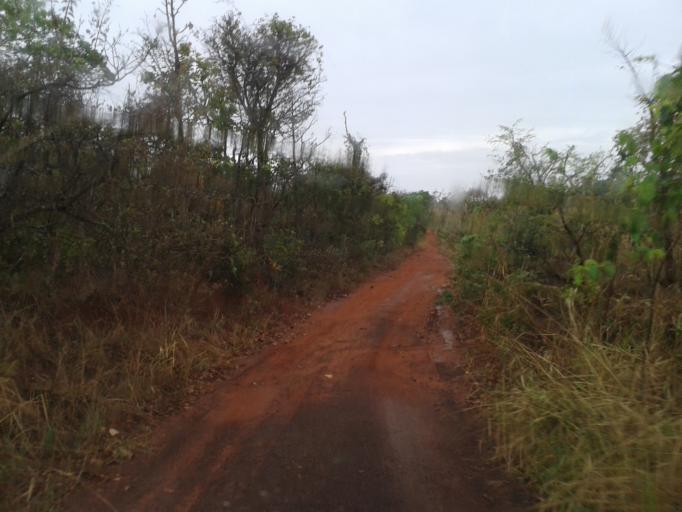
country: BR
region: Minas Gerais
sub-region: Campina Verde
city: Campina Verde
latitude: -19.3375
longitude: -49.5210
